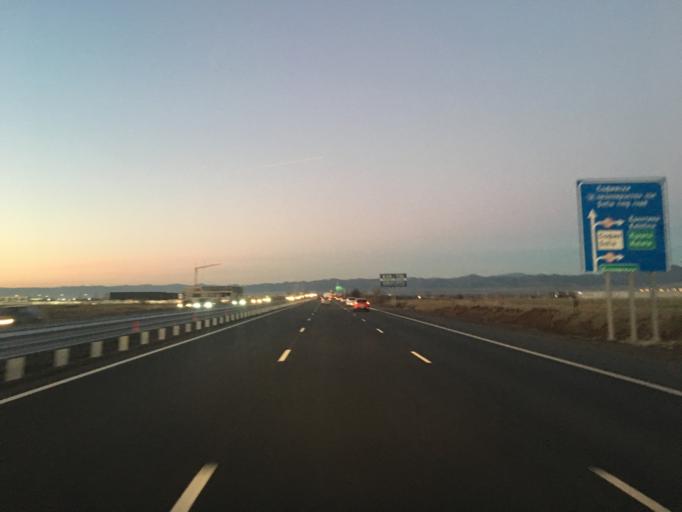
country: BG
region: Sofia-Capital
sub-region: Stolichna Obshtina
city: Sofia
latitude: 42.6995
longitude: 23.4512
